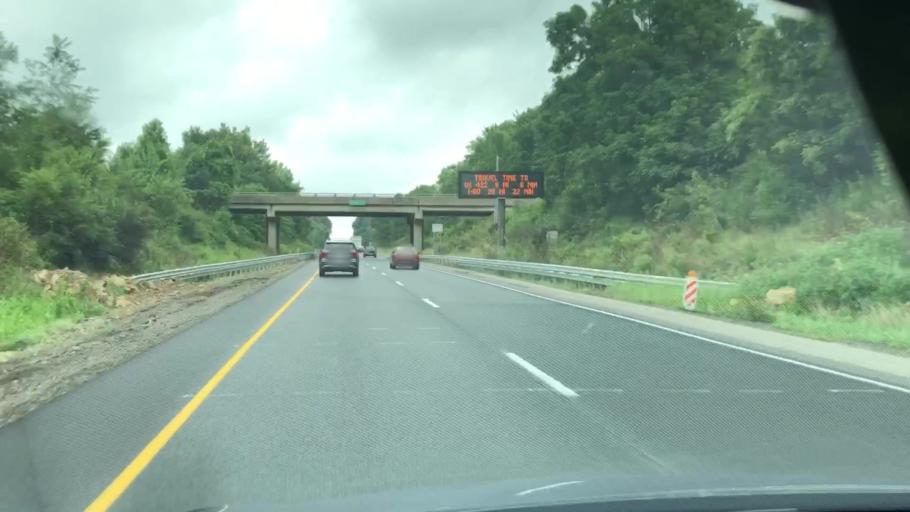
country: US
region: Pennsylvania
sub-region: Butler County
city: Prospect
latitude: 40.8871
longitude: -80.1174
